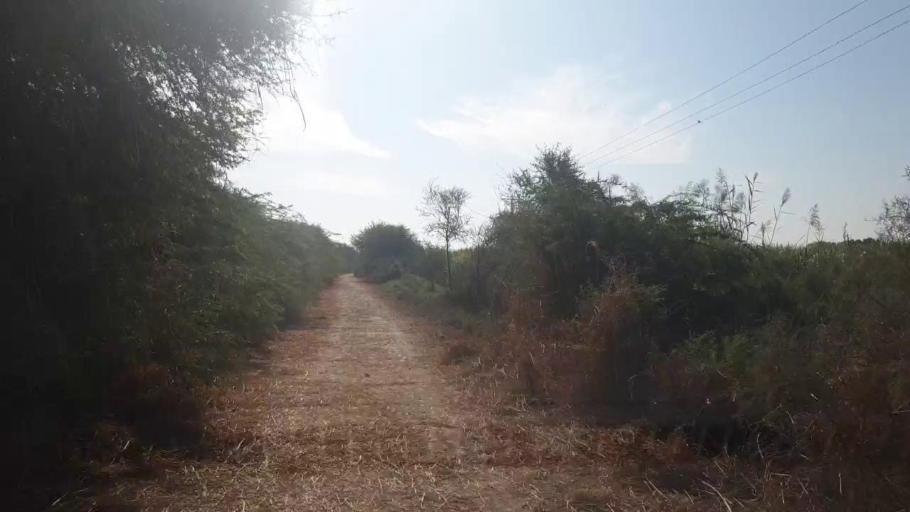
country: PK
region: Sindh
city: Talhar
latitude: 24.9375
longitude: 68.7992
